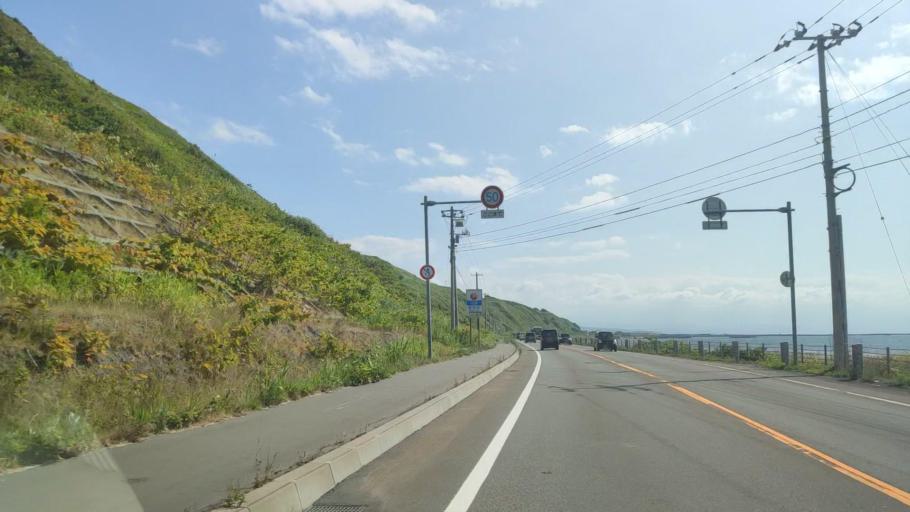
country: JP
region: Hokkaido
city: Rumoi
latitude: 43.9942
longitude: 141.6516
